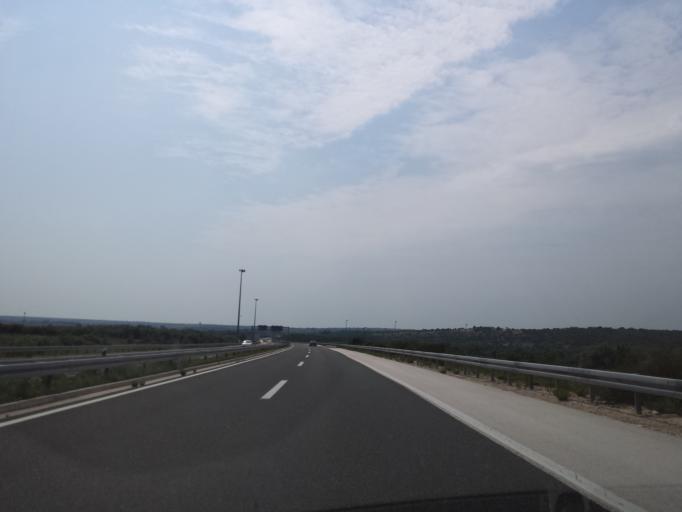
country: HR
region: Zadarska
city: Posedarje
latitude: 44.1880
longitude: 15.4335
